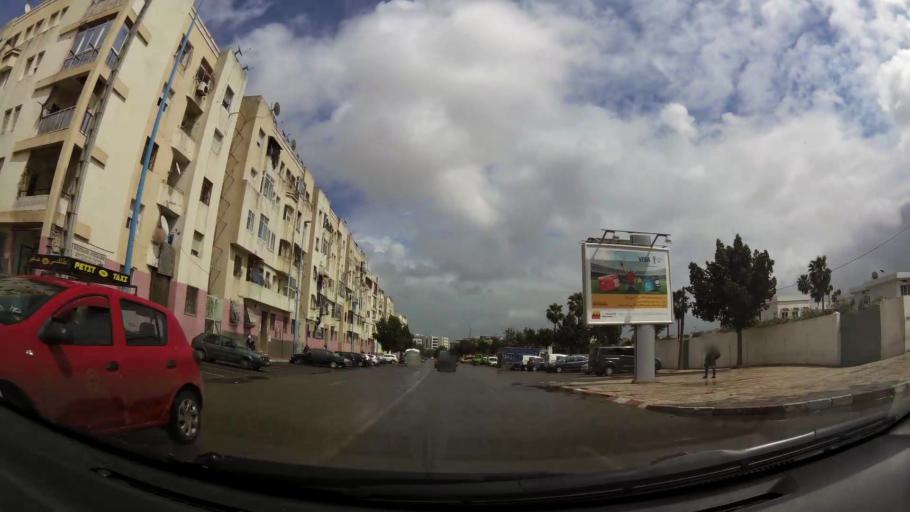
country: MA
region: Grand Casablanca
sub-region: Casablanca
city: Casablanca
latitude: 33.5246
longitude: -7.6494
